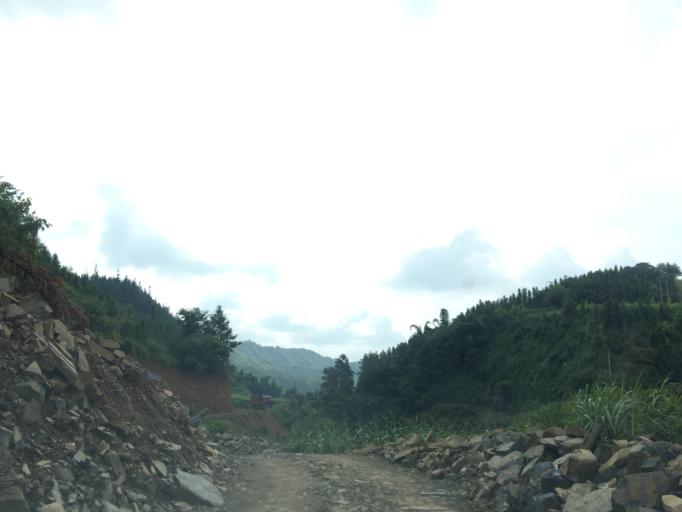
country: CN
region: Guangxi Zhuangzu Zizhiqu
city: Xinzhou
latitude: 24.8690
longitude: 105.8642
